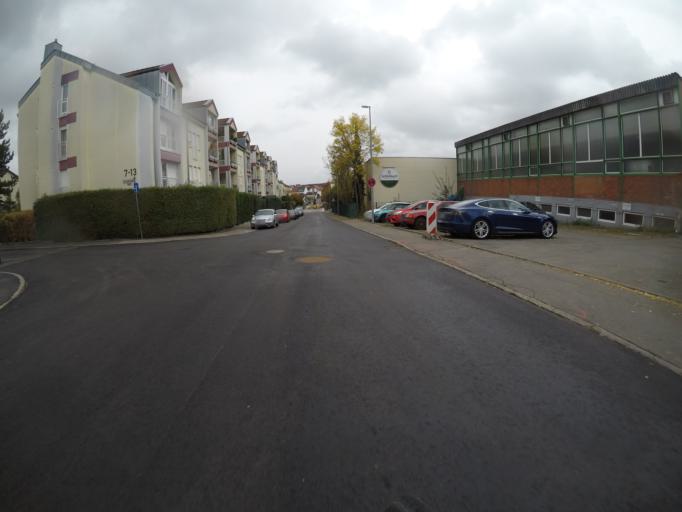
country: DE
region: Baden-Wuerttemberg
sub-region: Regierungsbezirk Stuttgart
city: Boeblingen
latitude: 48.6854
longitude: 9.0172
